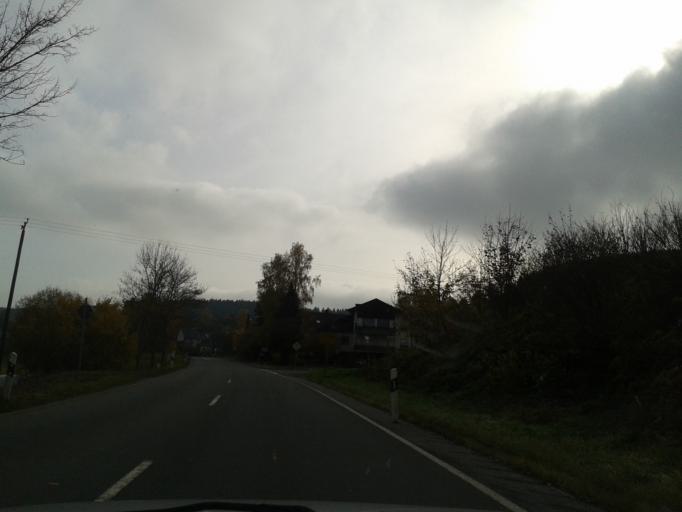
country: DE
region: North Rhine-Westphalia
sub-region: Regierungsbezirk Arnsberg
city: Bad Laasphe
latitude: 50.8781
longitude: 8.3480
